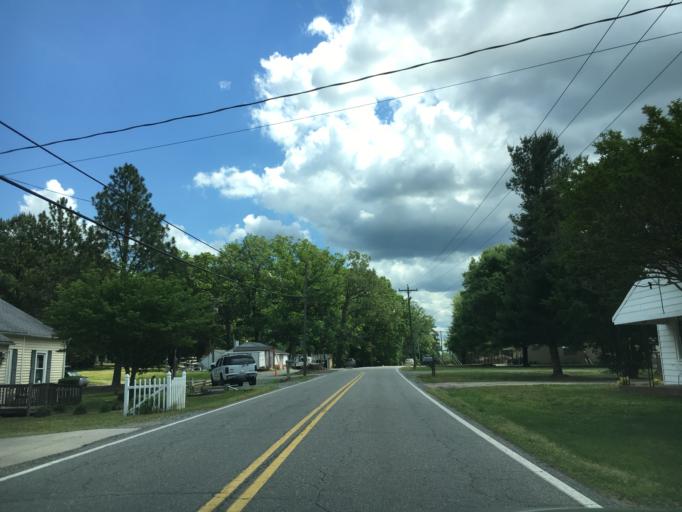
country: US
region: Virginia
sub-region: Halifax County
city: South Boston
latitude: 36.7045
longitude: -78.9261
